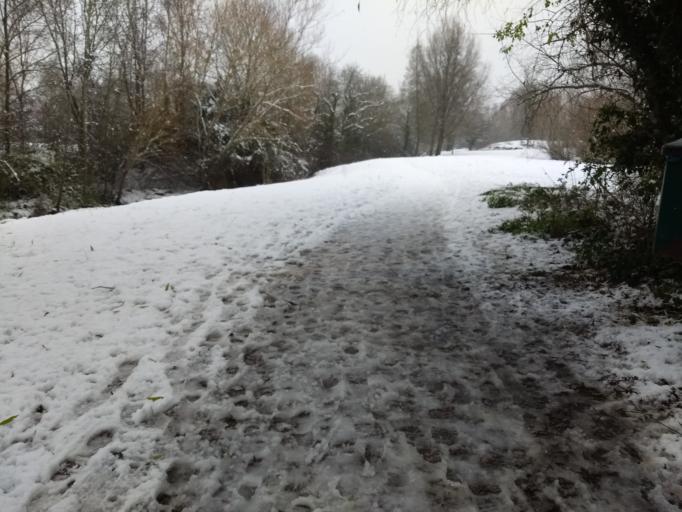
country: GB
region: England
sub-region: Milton Keynes
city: Shenley Church End
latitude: 52.0060
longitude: -0.7671
